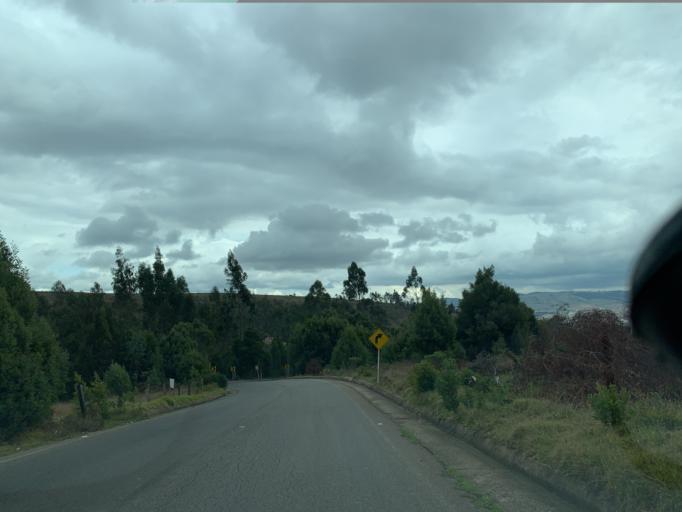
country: CO
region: Boyaca
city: Tunja
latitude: 5.5686
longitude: -73.3627
